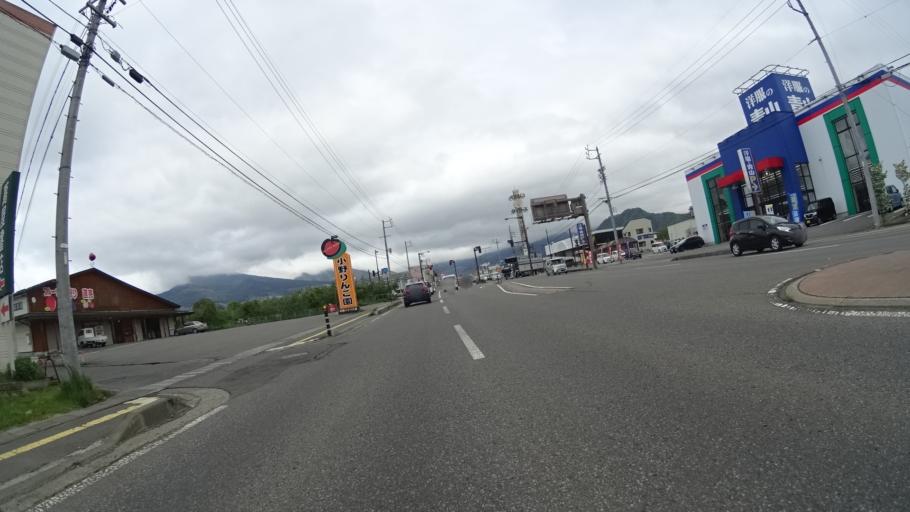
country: JP
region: Nagano
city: Nakano
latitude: 36.7551
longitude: 138.3572
